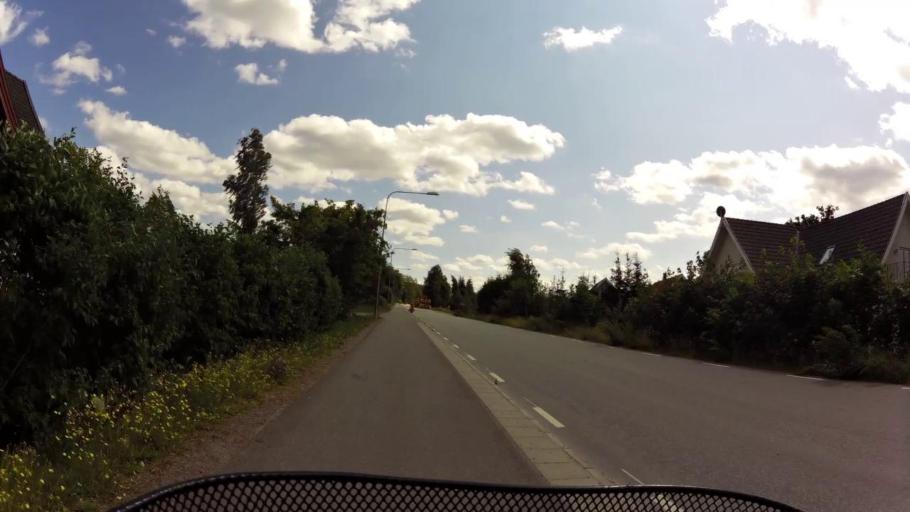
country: SE
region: OEstergoetland
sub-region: Linkopings Kommun
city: Ekangen
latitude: 58.4709
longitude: 15.6333
